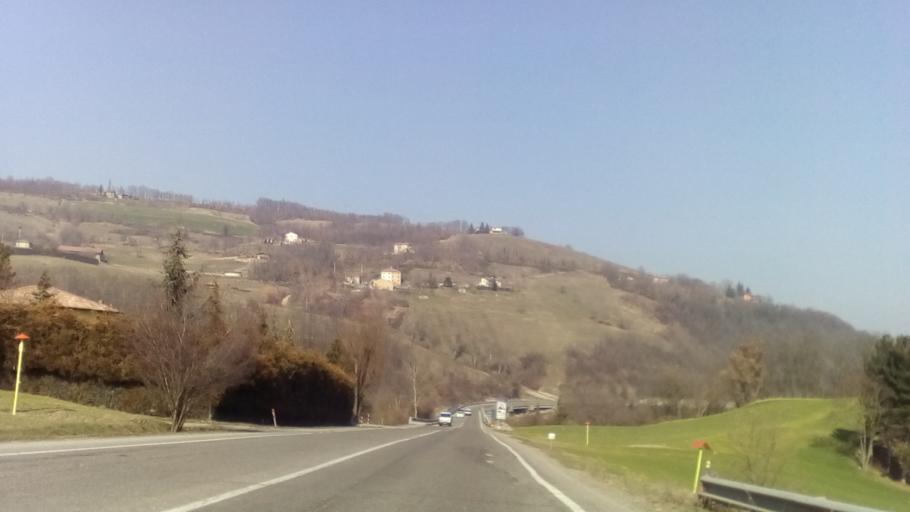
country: IT
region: Emilia-Romagna
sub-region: Provincia di Modena
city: Sant'Antonio
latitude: 44.4012
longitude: 10.8216
